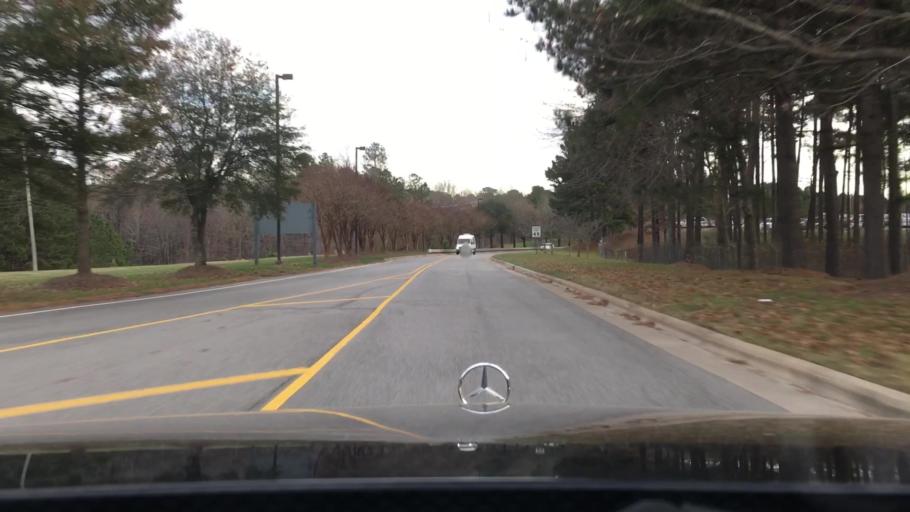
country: US
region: North Carolina
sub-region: Wake County
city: Morrisville
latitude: 35.8965
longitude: -78.7707
